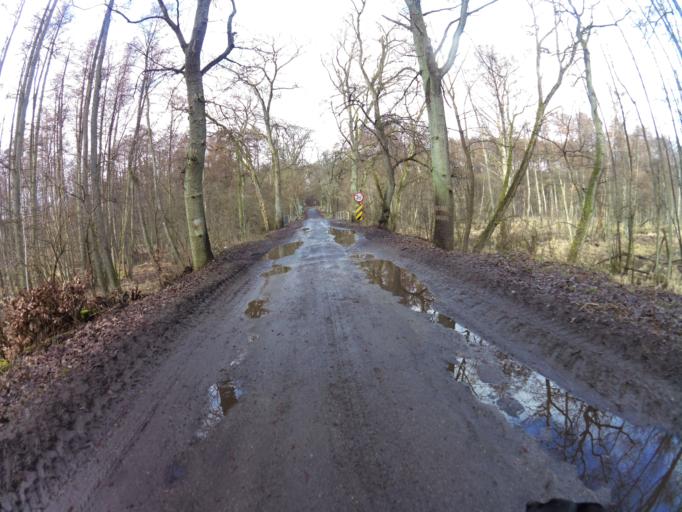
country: PL
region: West Pomeranian Voivodeship
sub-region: Powiat mysliborski
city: Debno
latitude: 52.7228
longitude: 14.7287
